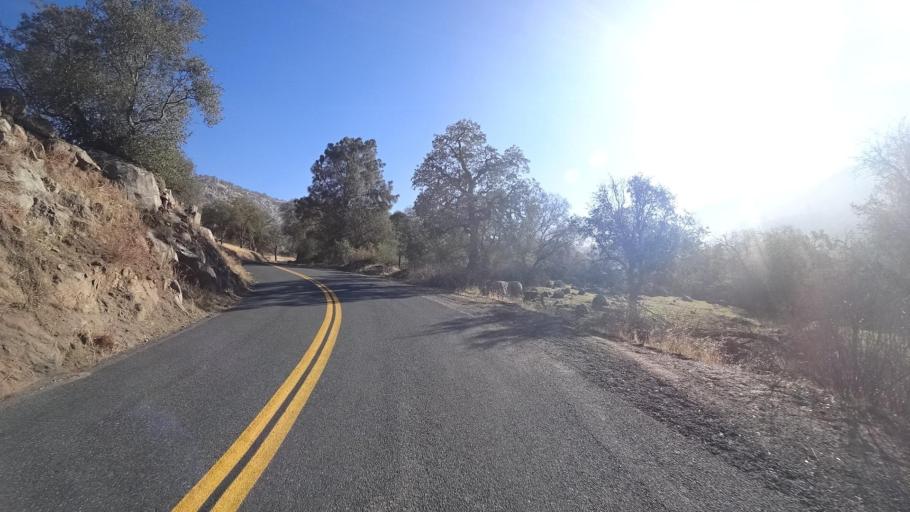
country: US
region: California
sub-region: Kern County
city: Alta Sierra
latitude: 35.7903
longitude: -118.8006
